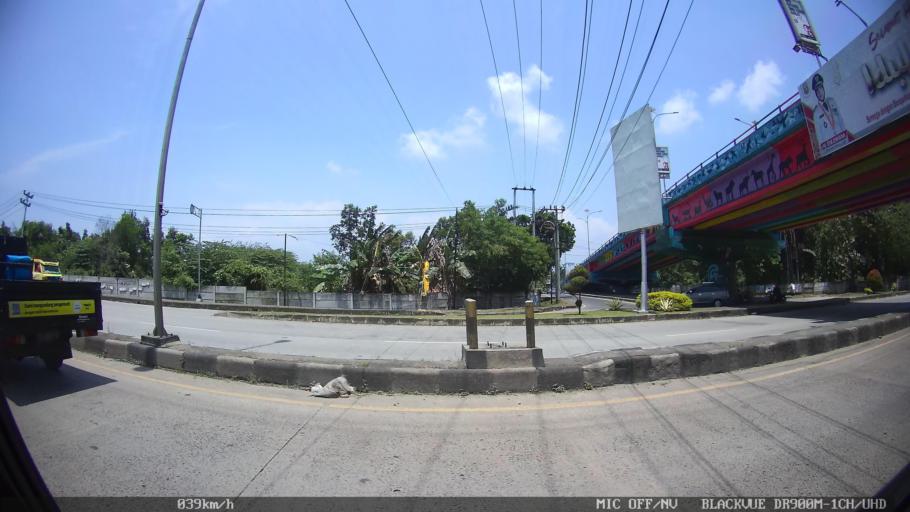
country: ID
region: Lampung
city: Kedaton
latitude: -5.3812
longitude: 105.2852
